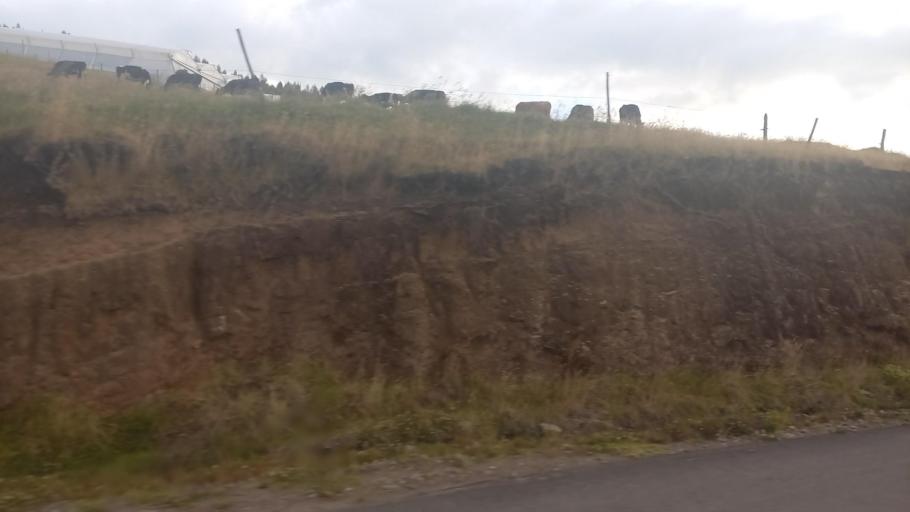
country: EC
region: Pichincha
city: Cayambe
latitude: 0.1026
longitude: -78.0827
